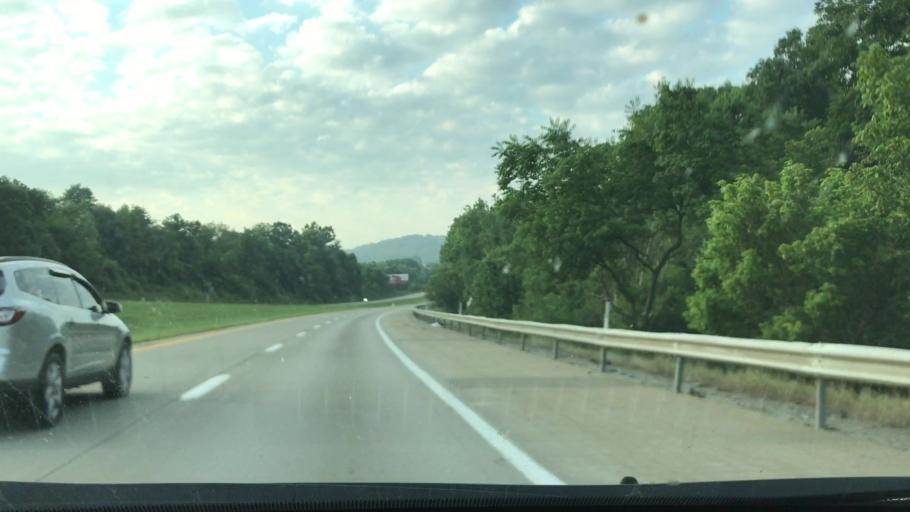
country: US
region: Pennsylvania
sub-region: Greene County
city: Morrisville
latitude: 39.9085
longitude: -80.1532
